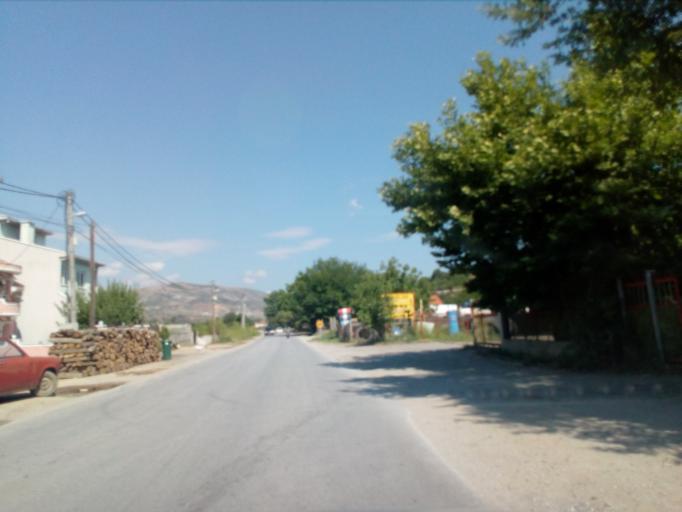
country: MK
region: Veles
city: Veles
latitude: 41.7263
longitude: 21.7830
